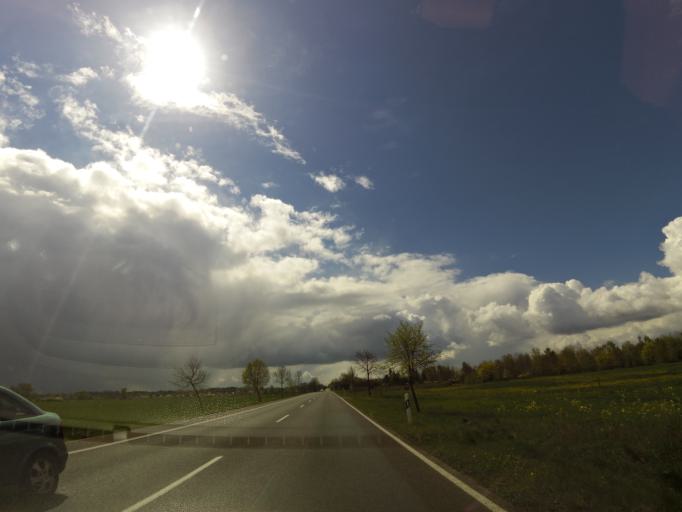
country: DE
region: Saxony-Anhalt
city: Biederitz
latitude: 52.1517
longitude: 11.7379
